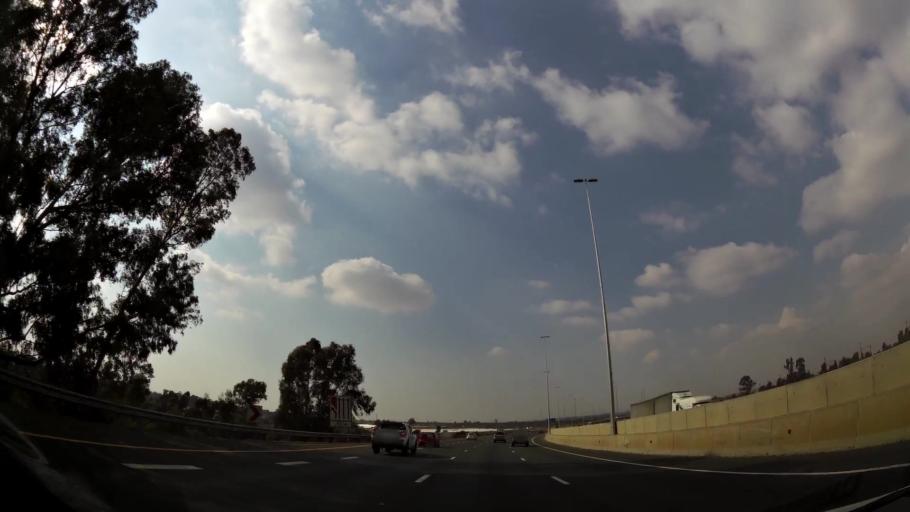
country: ZA
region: Gauteng
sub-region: Ekurhuleni Metropolitan Municipality
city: Benoni
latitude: -26.1628
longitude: 28.3632
